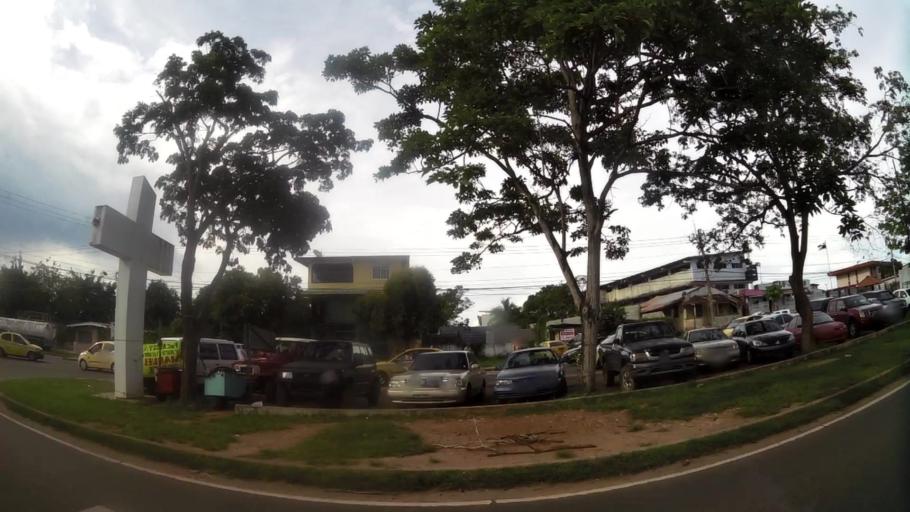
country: PA
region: Panama
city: La Chorrera
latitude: 8.8743
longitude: -79.7910
